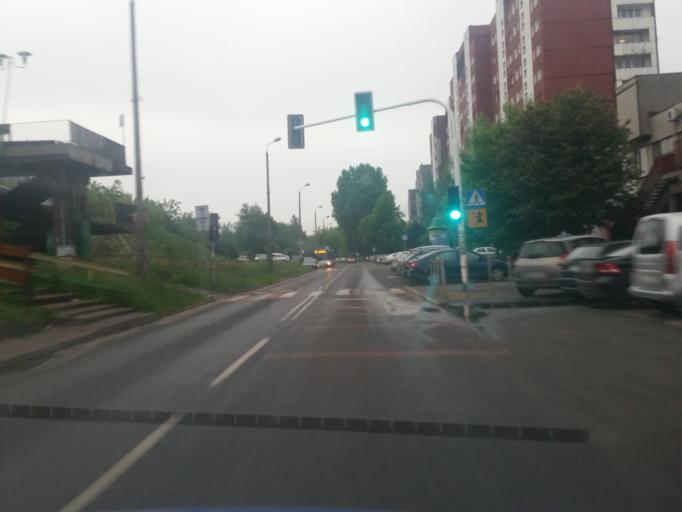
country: PL
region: Silesian Voivodeship
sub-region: Sosnowiec
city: Sosnowiec
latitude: 50.2695
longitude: 19.1234
